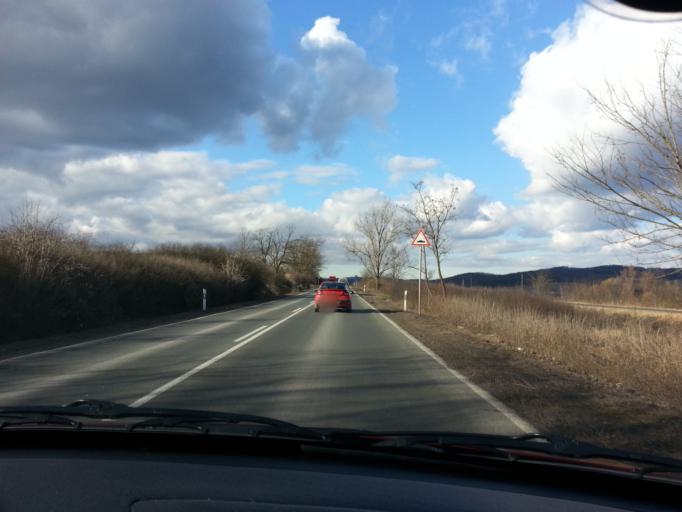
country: HU
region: Nograd
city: Kazar
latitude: 48.0273
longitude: 19.8142
